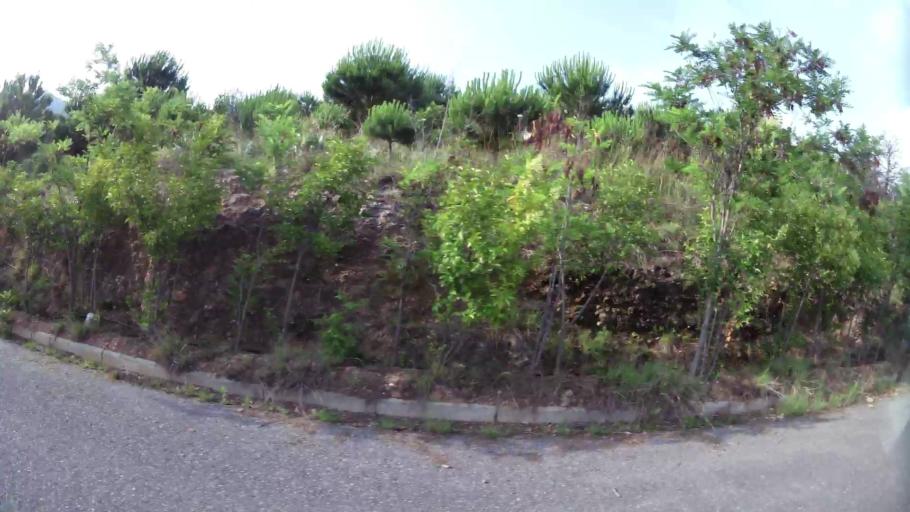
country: GR
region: Central Macedonia
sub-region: Nomos Thessalonikis
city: Oraiokastro
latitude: 40.7260
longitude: 22.9045
